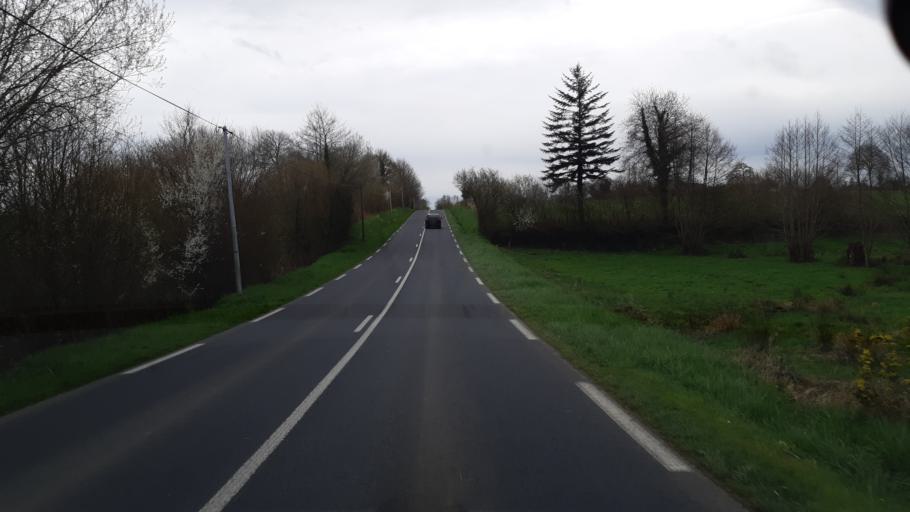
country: FR
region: Lower Normandy
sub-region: Departement de la Manche
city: Tessy-sur-Vire
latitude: 49.0217
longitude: -1.1466
